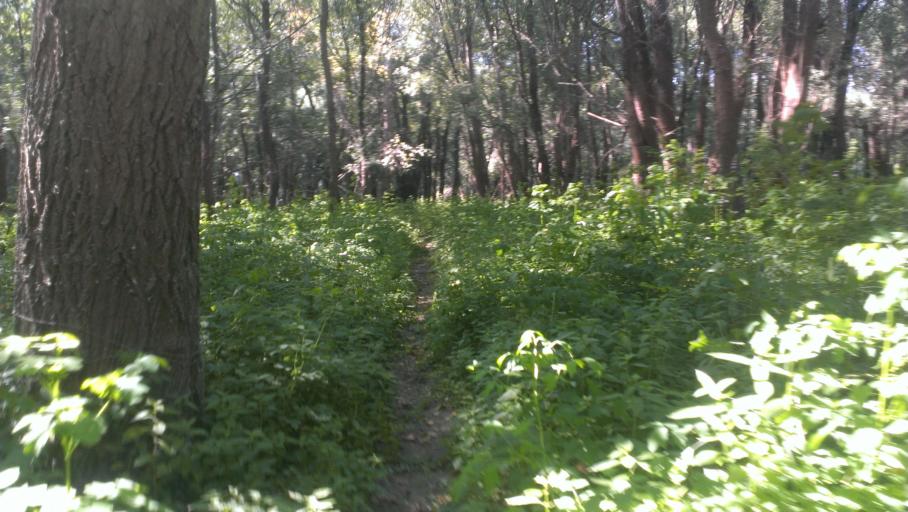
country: RU
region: Altai Krai
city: Nauchnyy Gorodok
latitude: 53.4321
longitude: 83.5101
